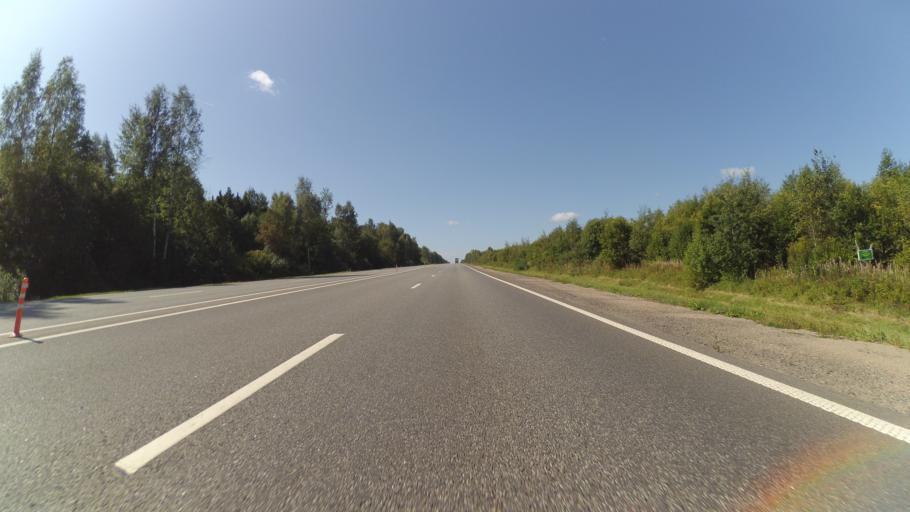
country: RU
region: Smolensk
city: Katyn'
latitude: 54.7865
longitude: 31.5705
